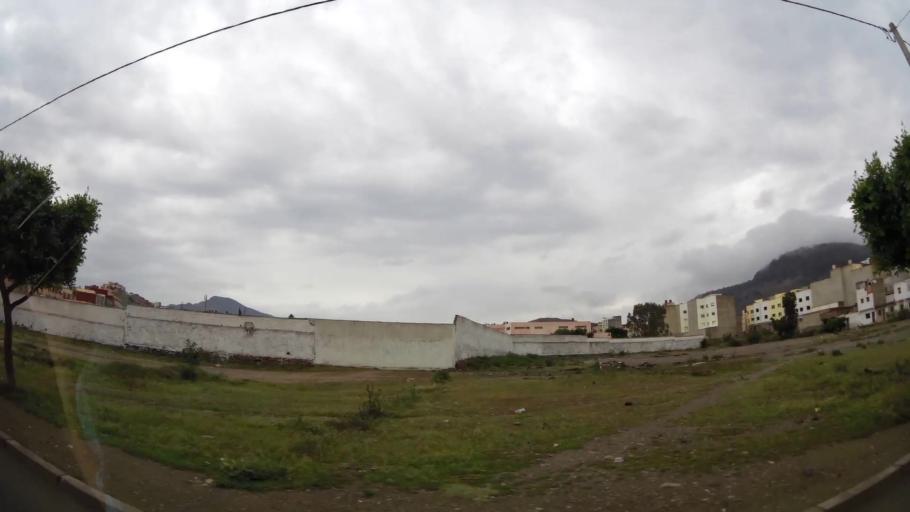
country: MA
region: Oriental
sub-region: Nador
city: Nador
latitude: 35.1519
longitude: -2.9988
